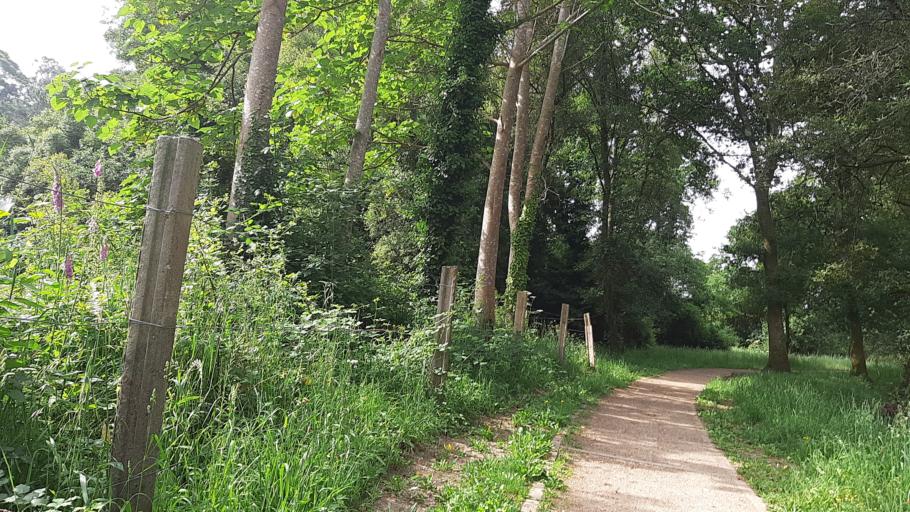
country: ES
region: Galicia
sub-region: Provincia de Pontevedra
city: O Rosal
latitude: 41.9220
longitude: -8.8256
